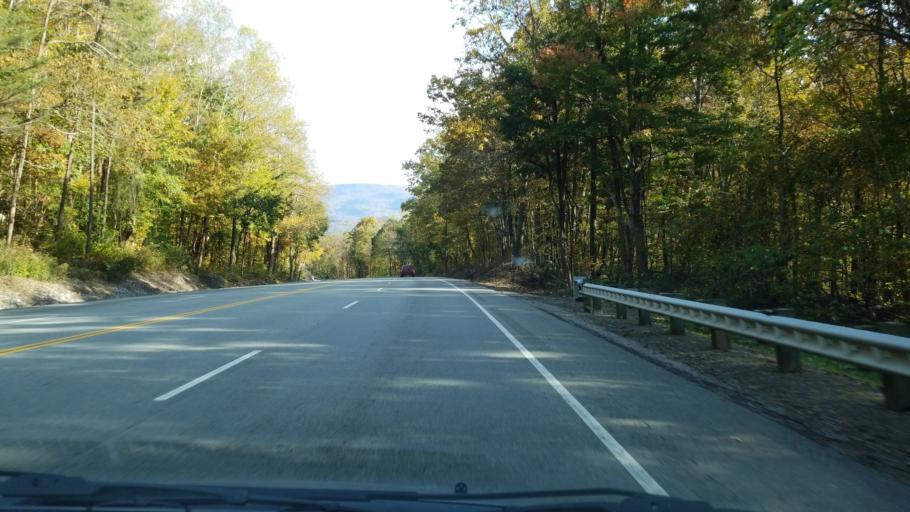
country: US
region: Tennessee
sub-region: Sequatchie County
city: Dunlap
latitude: 35.4078
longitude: -85.4014
